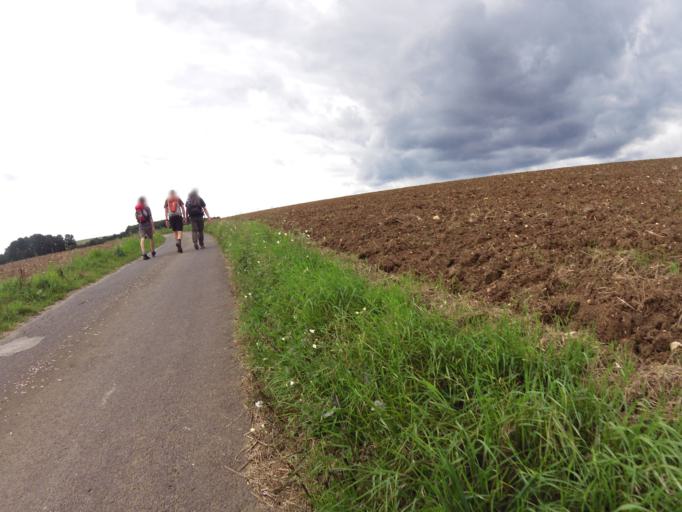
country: DE
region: Rheinland-Pfalz
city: Odernheim
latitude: 49.7609
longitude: 7.6870
